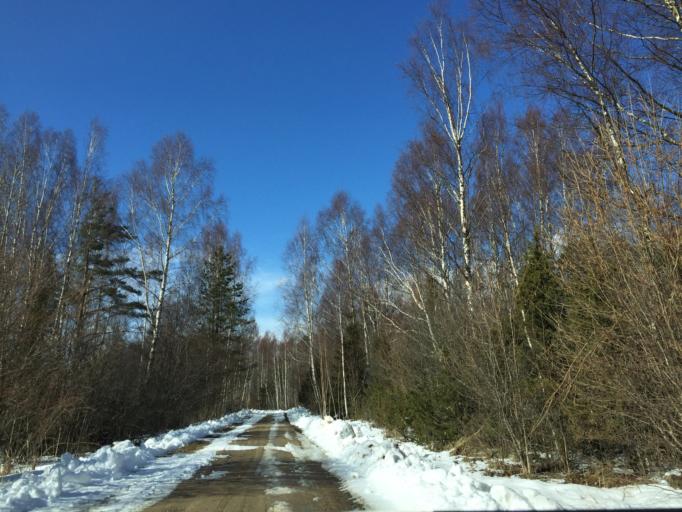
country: EE
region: Saare
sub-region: Orissaare vald
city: Orissaare
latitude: 58.3983
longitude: 22.9758
